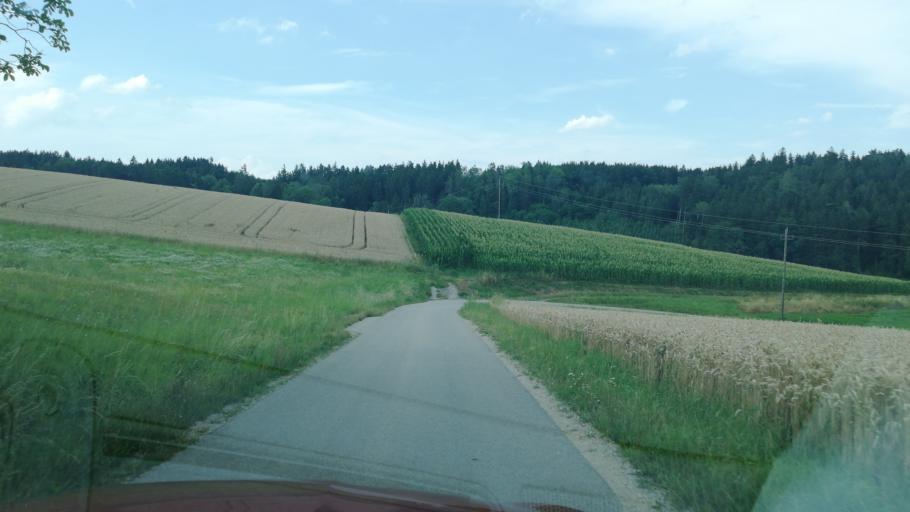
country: AT
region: Upper Austria
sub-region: Wels-Land
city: Neukirchen bei Lambach
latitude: 48.1126
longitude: 13.8233
